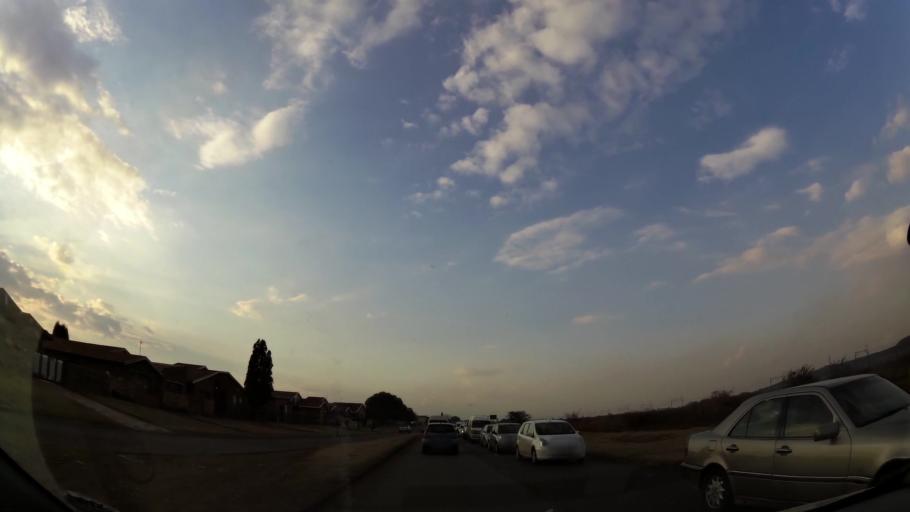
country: ZA
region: Gauteng
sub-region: Sedibeng District Municipality
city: Vereeniging
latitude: -26.5928
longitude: 27.8506
